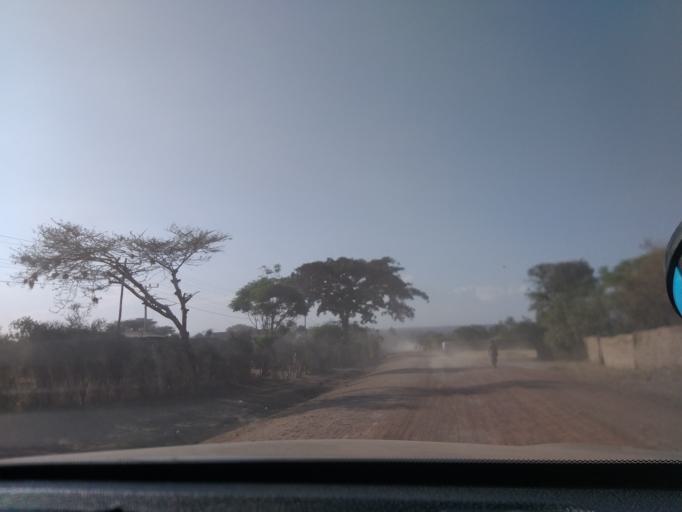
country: ET
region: Oromiya
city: Shashemene
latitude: 7.4866
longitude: 38.7485
